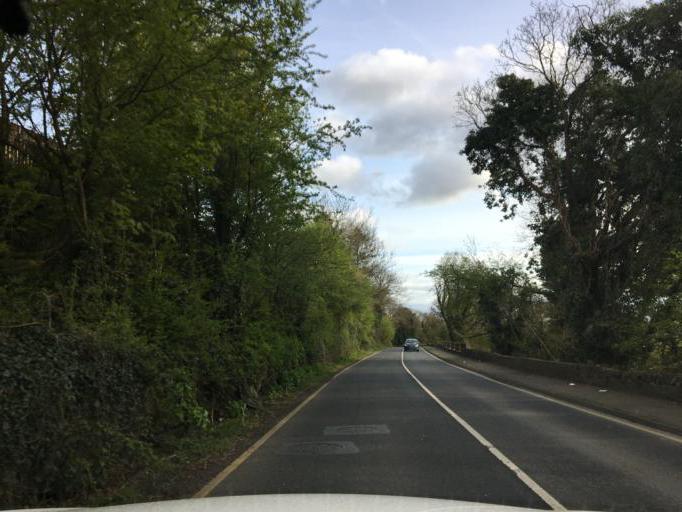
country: IE
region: Leinster
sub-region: Loch Garman
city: New Ross
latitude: 52.4072
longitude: -6.9383
